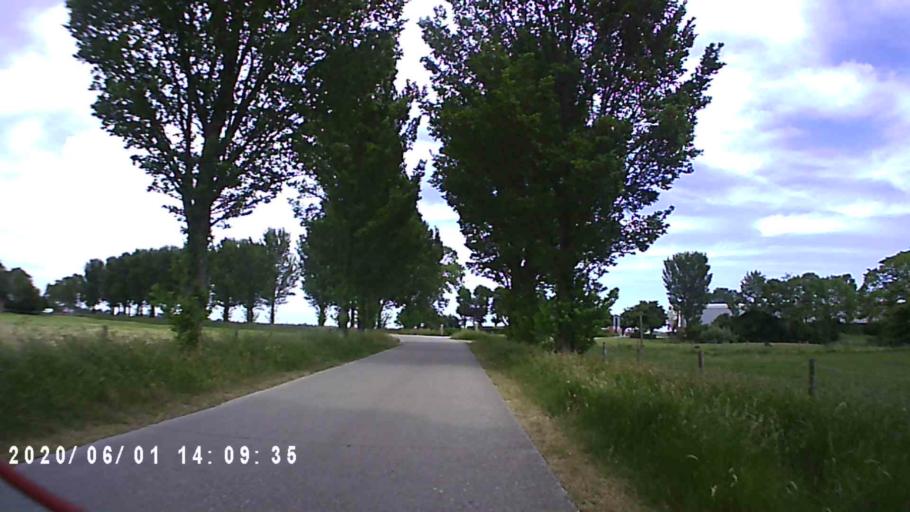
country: NL
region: Friesland
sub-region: Gemeente Littenseradiel
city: Winsum
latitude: 53.1225
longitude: 5.6470
